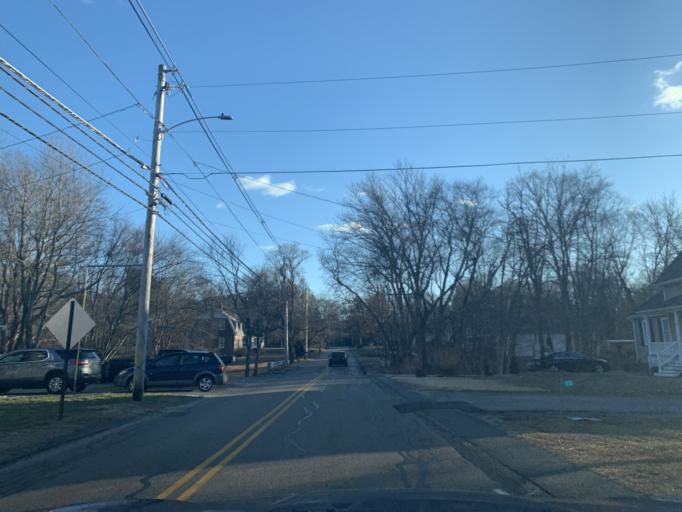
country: US
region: Massachusetts
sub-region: Bristol County
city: Norton
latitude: 41.9426
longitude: -71.2028
